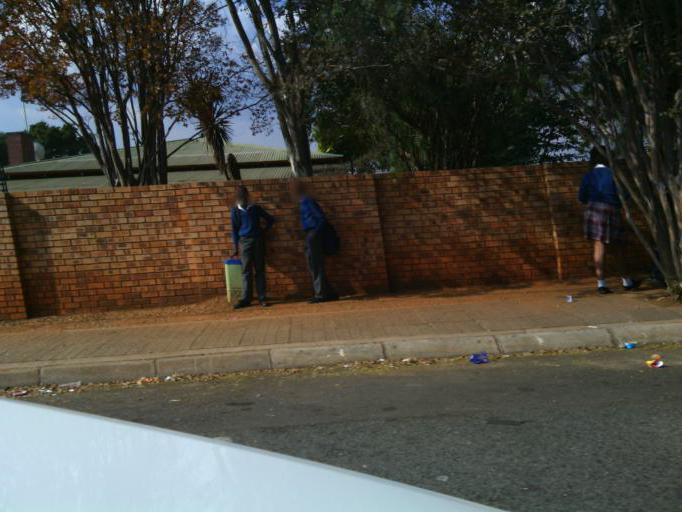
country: ZA
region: Gauteng
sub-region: City of Tshwane Metropolitan Municipality
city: Centurion
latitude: -25.8341
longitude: 28.2013
